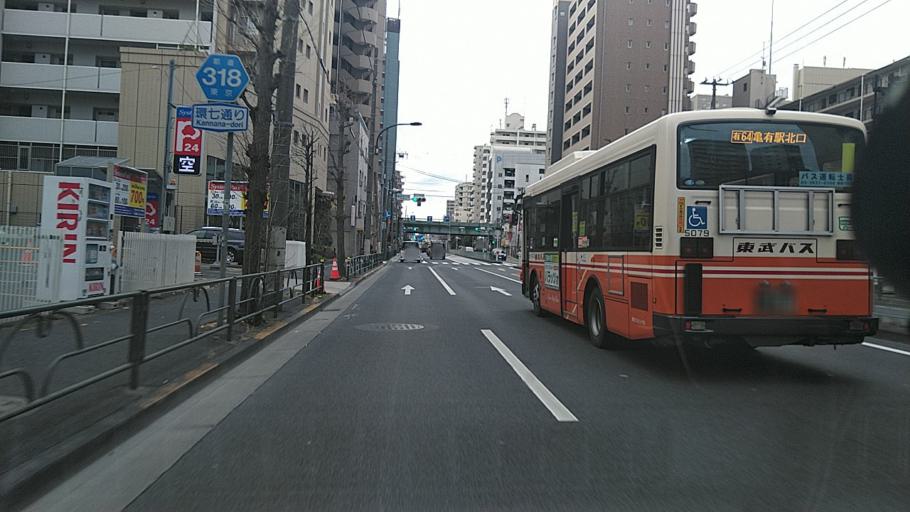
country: JP
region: Chiba
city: Matsudo
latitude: 35.7688
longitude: 139.8491
